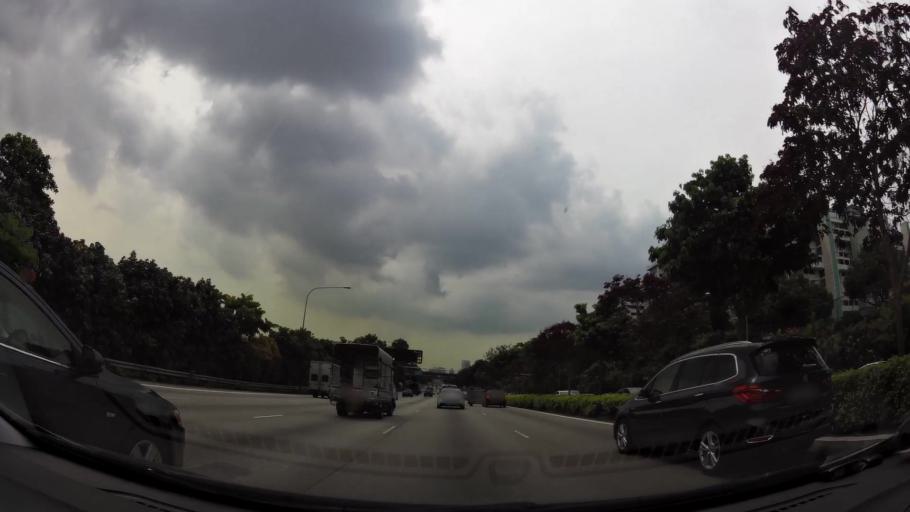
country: SG
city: Singapore
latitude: 1.3635
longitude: 103.8593
